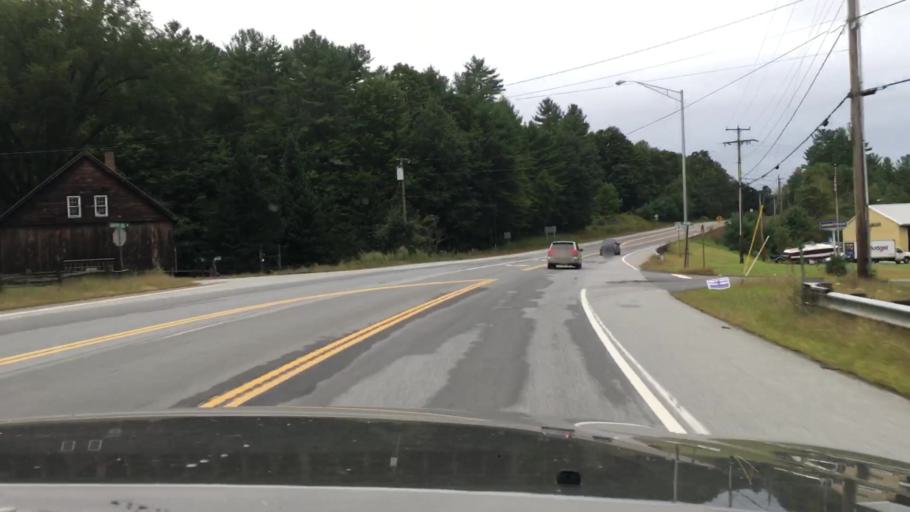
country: US
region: New Hampshire
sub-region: Cheshire County
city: Chesterfield
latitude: 42.8958
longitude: -72.5110
